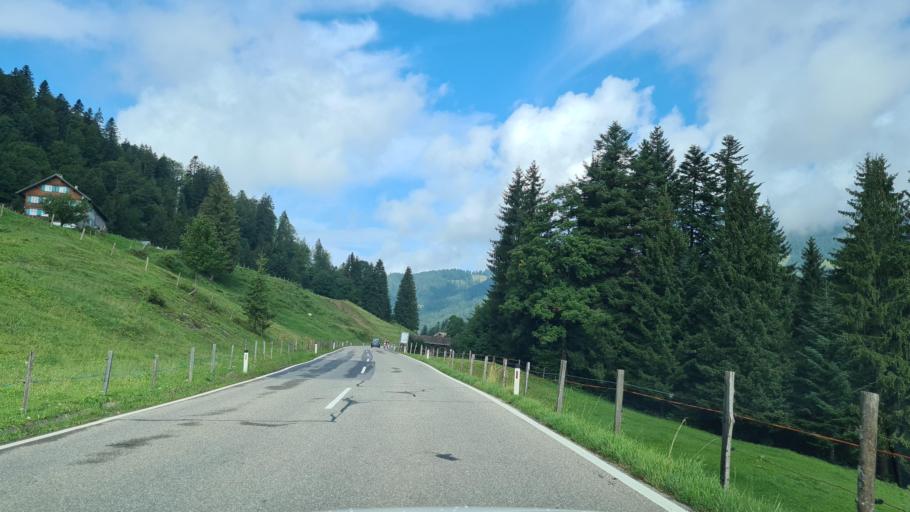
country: AT
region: Vorarlberg
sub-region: Politischer Bezirk Bregenz
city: Sibratsgfall
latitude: 47.4519
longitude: 10.0022
